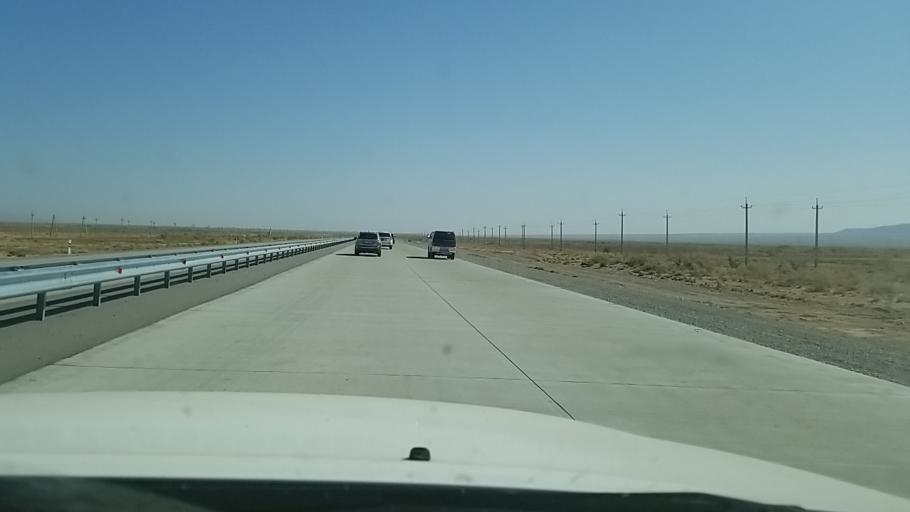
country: KZ
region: Almaty Oblysy
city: Kegen
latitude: 43.7314
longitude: 78.7861
